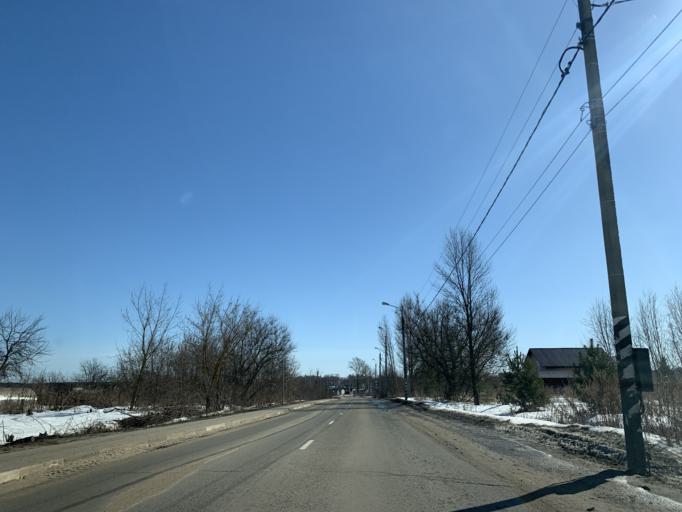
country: RU
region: Jaroslavl
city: Konstantinovskiy
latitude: 57.8376
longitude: 39.5847
